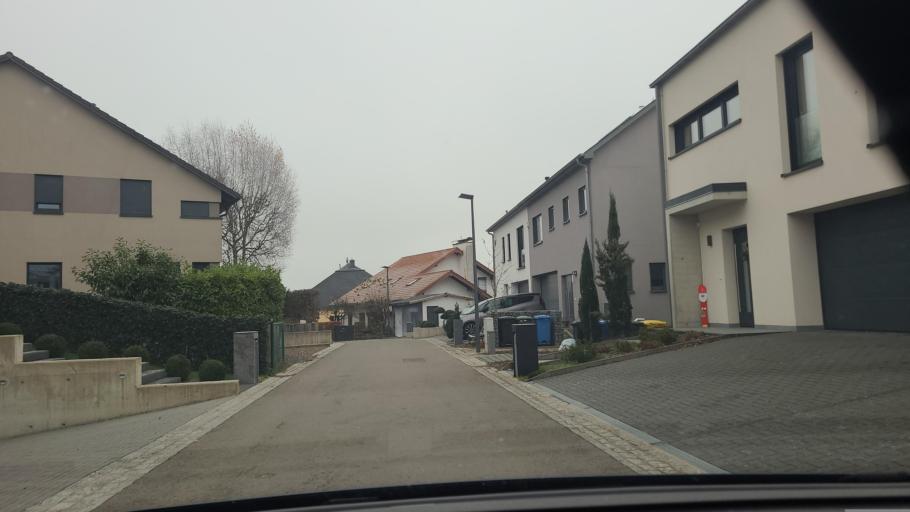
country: LU
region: Luxembourg
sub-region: Canton de Capellen
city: Garnich
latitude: 49.6192
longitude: 5.9550
